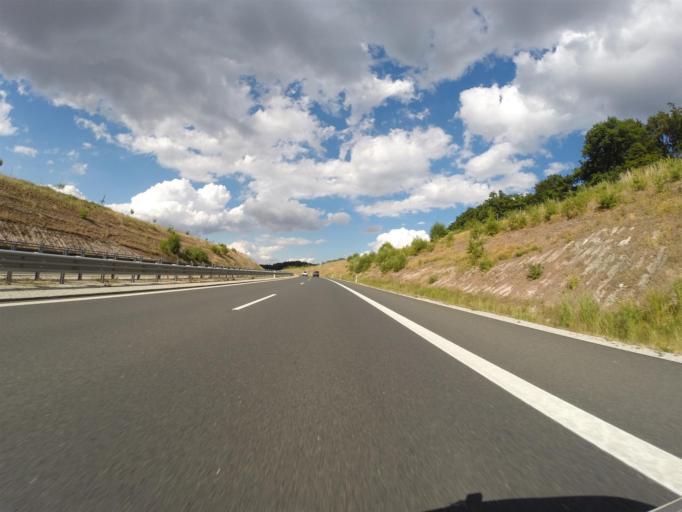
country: DE
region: Bavaria
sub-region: Upper Franconia
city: Untersiemau
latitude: 50.1788
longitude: 11.0208
